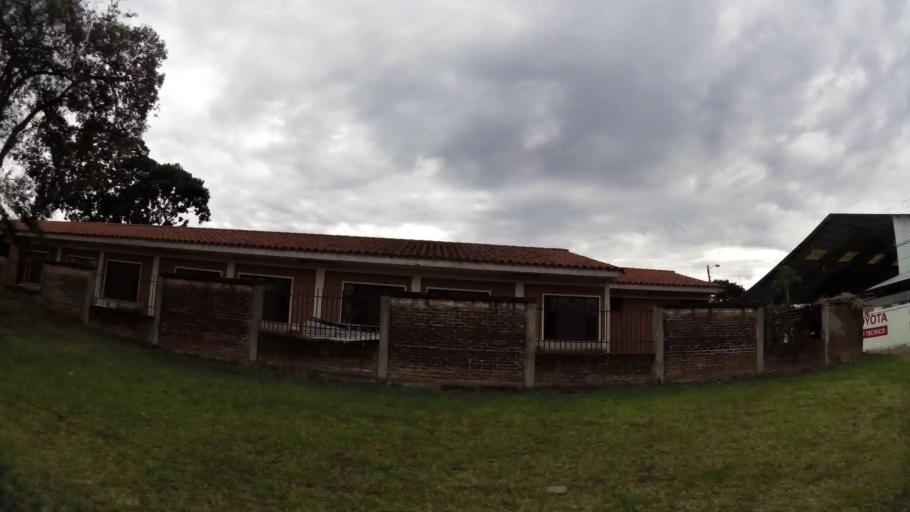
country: BO
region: Santa Cruz
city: Santa Cruz de la Sierra
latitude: -17.7535
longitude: -63.1791
